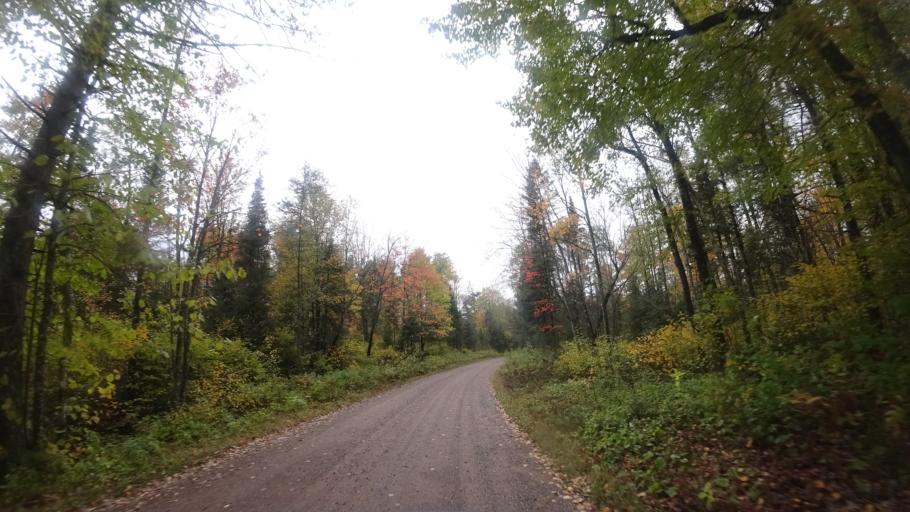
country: US
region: Wisconsin
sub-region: Sawyer County
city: Little Round Lake
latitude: 46.0499
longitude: -90.9926
